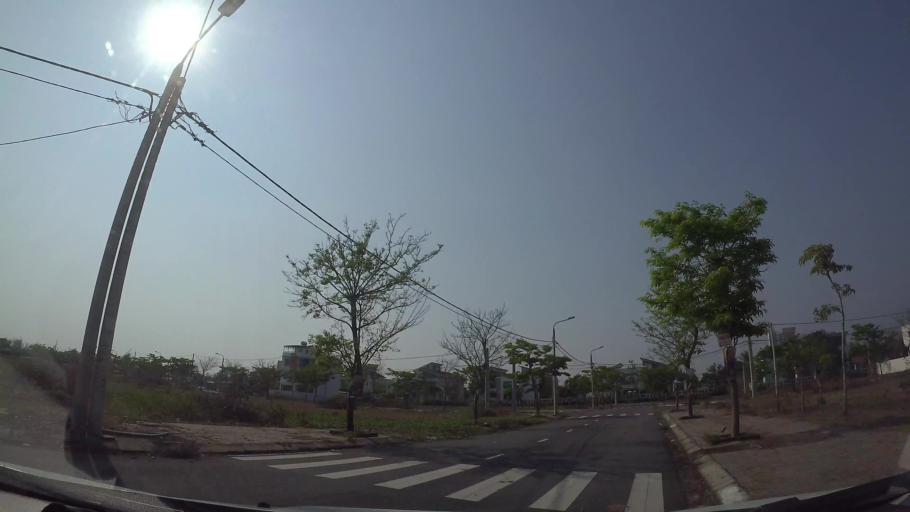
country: VN
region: Da Nang
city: Ngu Hanh Son
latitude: 15.9561
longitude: 108.2814
